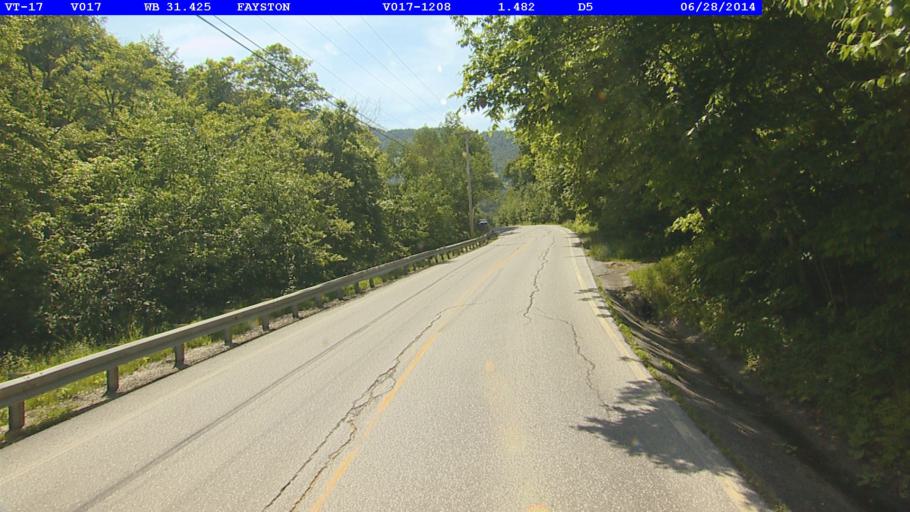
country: US
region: Vermont
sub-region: Addison County
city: Bristol
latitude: 44.2019
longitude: -72.9124
